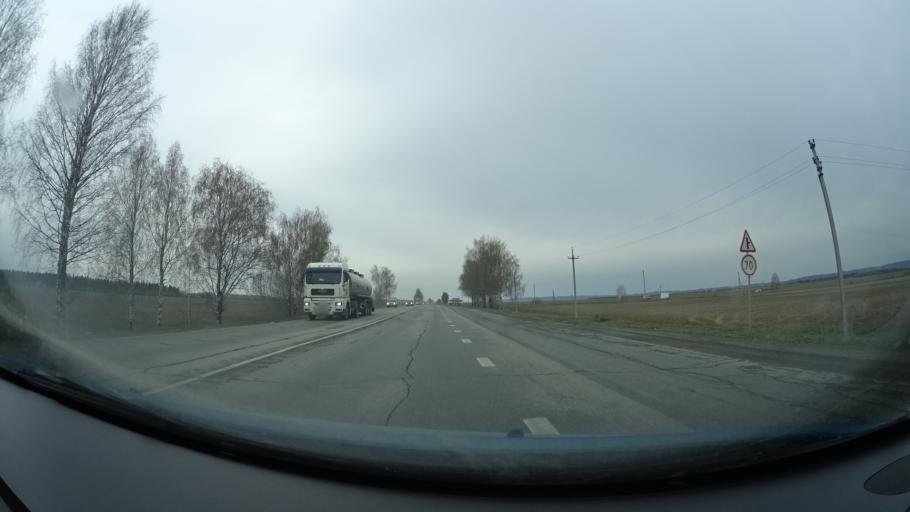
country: RU
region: Perm
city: Ust'-Kachka
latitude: 58.0702
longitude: 55.6312
